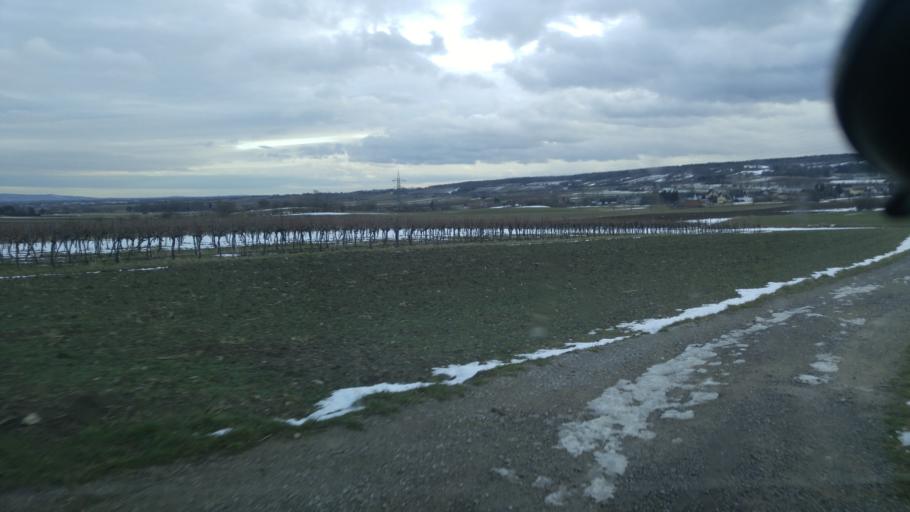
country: AT
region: Lower Austria
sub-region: Politischer Bezirk Baden
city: Hirtenberg
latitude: 47.9637
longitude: 16.1688
